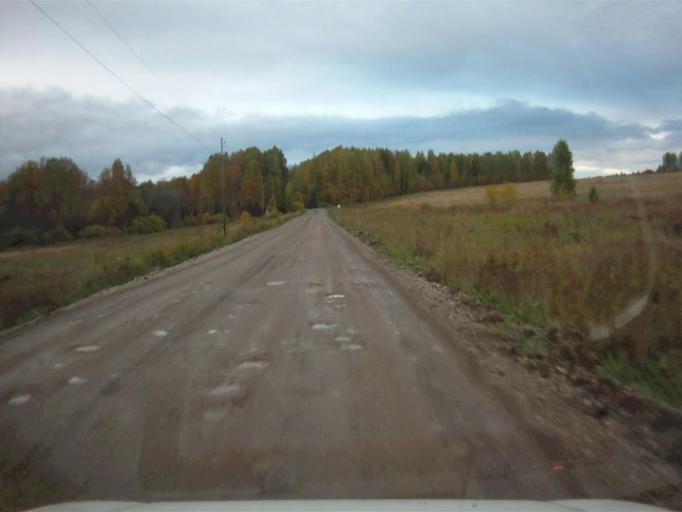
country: RU
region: Sverdlovsk
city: Mikhaylovsk
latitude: 56.1914
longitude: 59.1904
